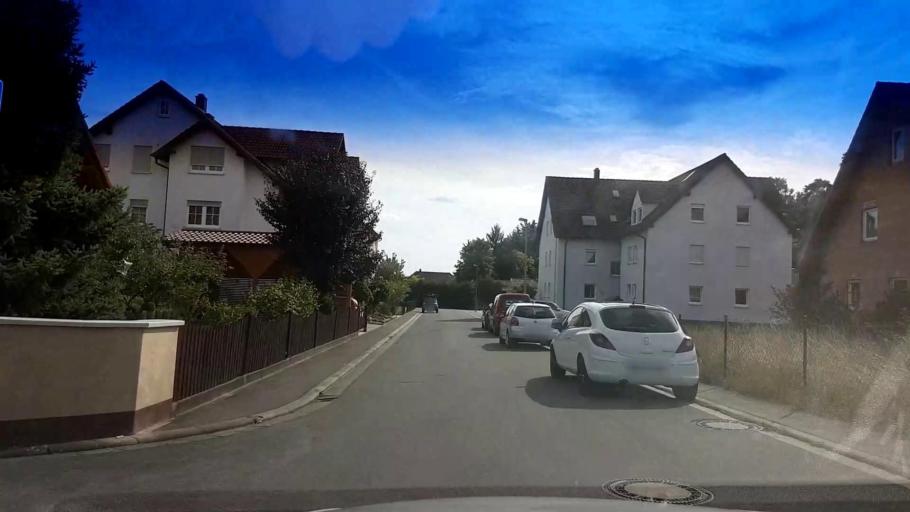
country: DE
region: Bavaria
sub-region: Upper Franconia
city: Oberhaid
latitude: 49.9372
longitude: 10.8063
